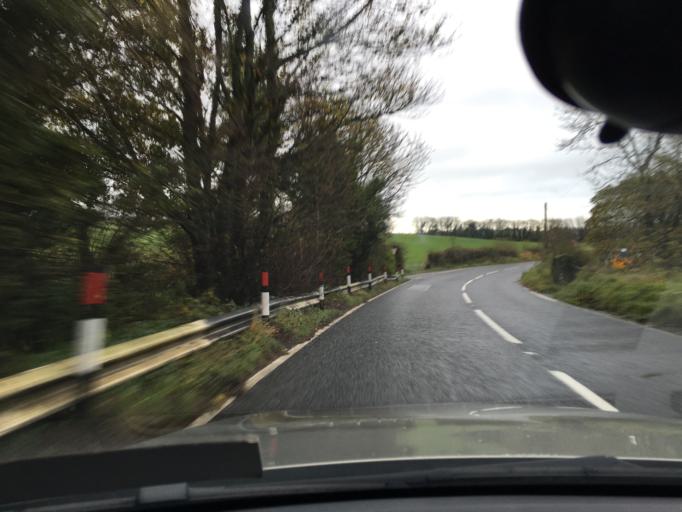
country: GB
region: Northern Ireland
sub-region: Larne District
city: Larne
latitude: 54.8350
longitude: -5.8797
